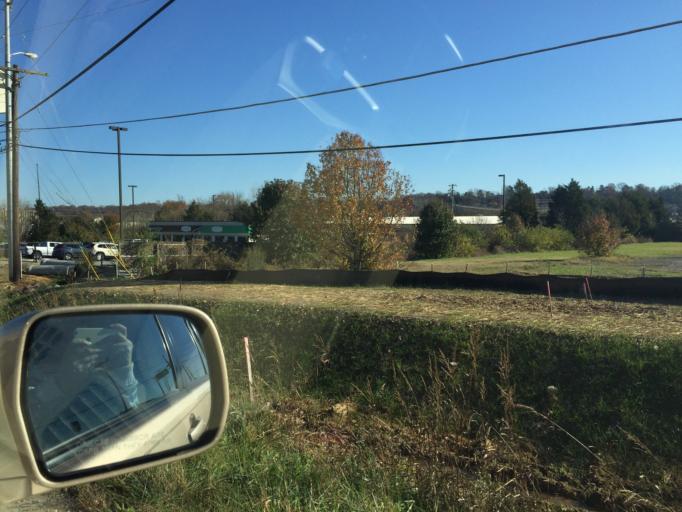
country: US
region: Tennessee
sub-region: Knox County
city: Farragut
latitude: 35.9122
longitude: -84.1072
